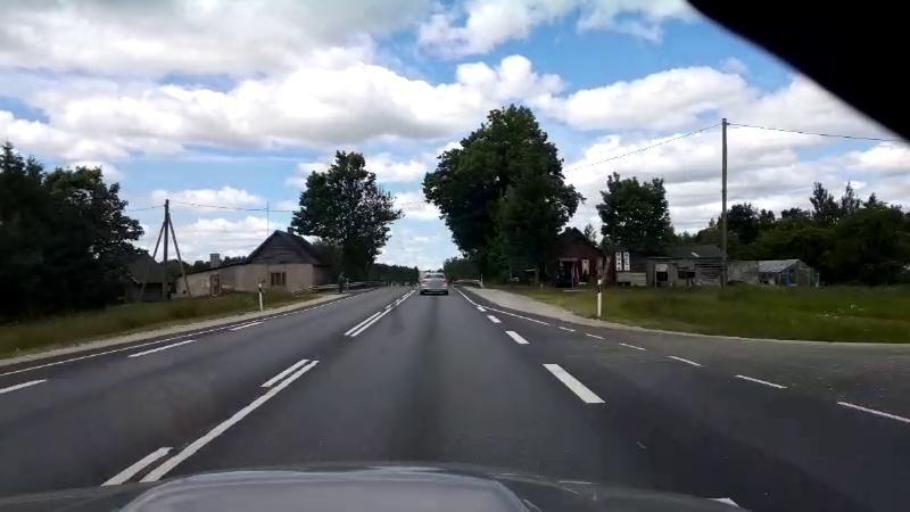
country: EE
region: Paernumaa
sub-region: Halinga vald
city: Parnu-Jaagupi
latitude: 58.6703
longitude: 24.4506
